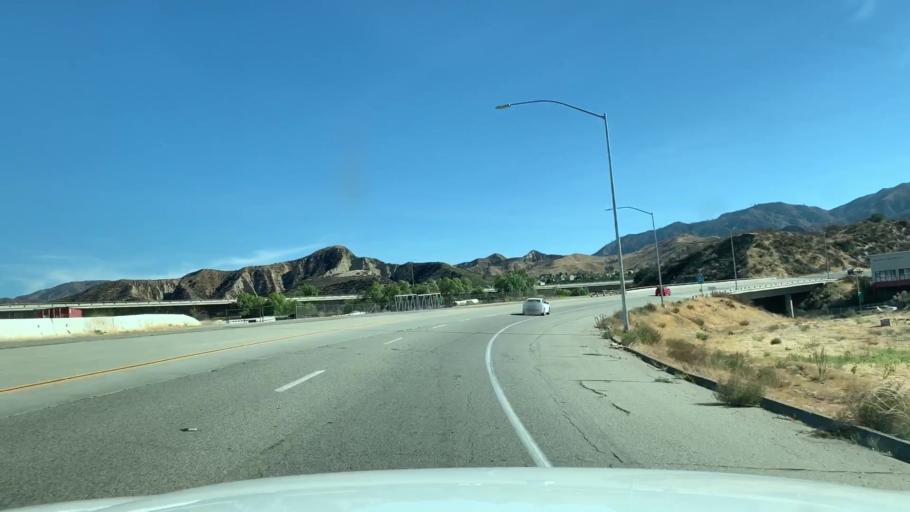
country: US
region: California
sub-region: Los Angeles County
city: Santa Clarita
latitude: 34.4045
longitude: -118.4584
